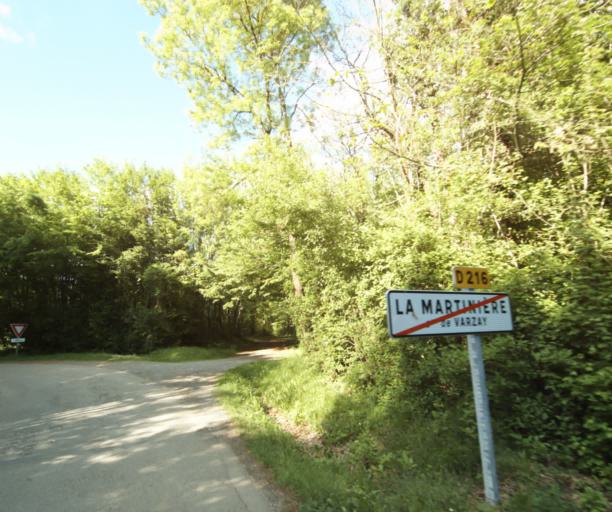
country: FR
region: Poitou-Charentes
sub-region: Departement de la Charente-Maritime
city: Nieul-les-Saintes
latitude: 45.7089
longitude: -0.7512
